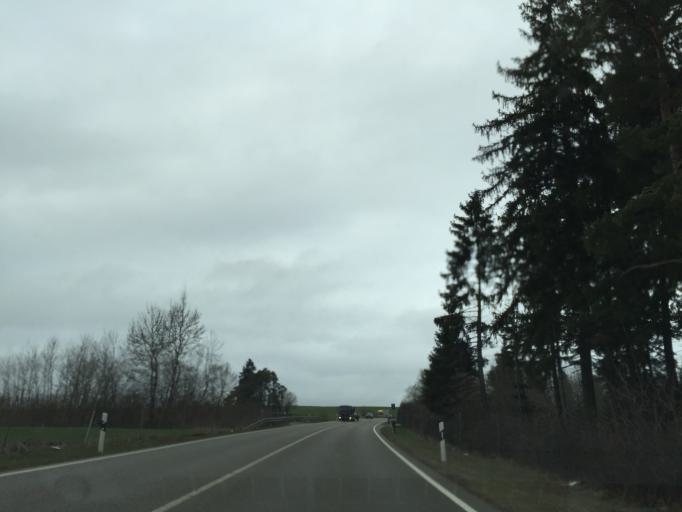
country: DE
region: Baden-Wuerttemberg
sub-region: Freiburg Region
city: Villingen-Schwenningen
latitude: 48.0394
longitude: 8.4914
